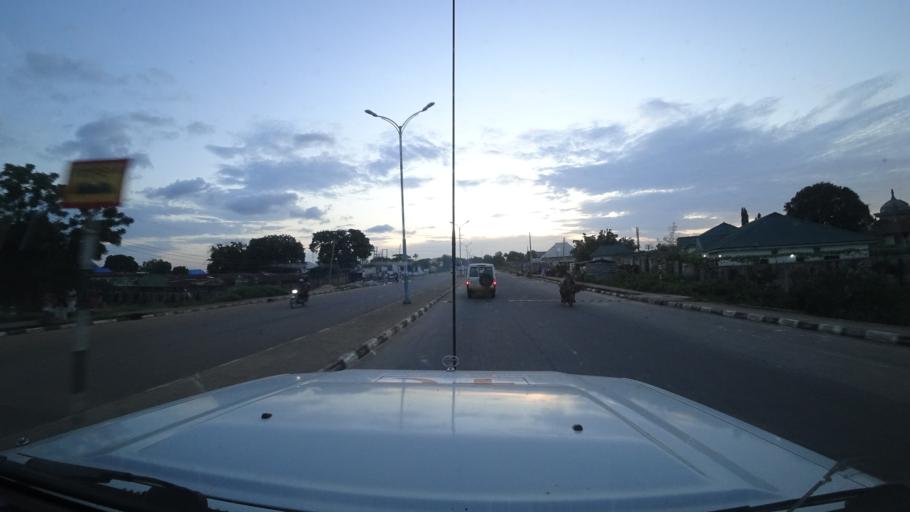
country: NG
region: Niger
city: Minna
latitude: 9.6407
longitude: 6.5460
